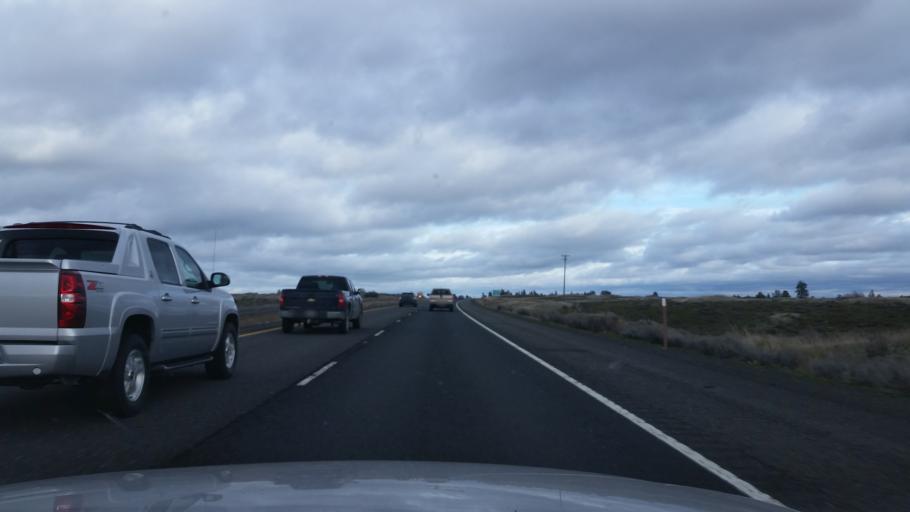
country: US
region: Washington
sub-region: Spokane County
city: Medical Lake
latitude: 47.3824
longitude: -117.8630
